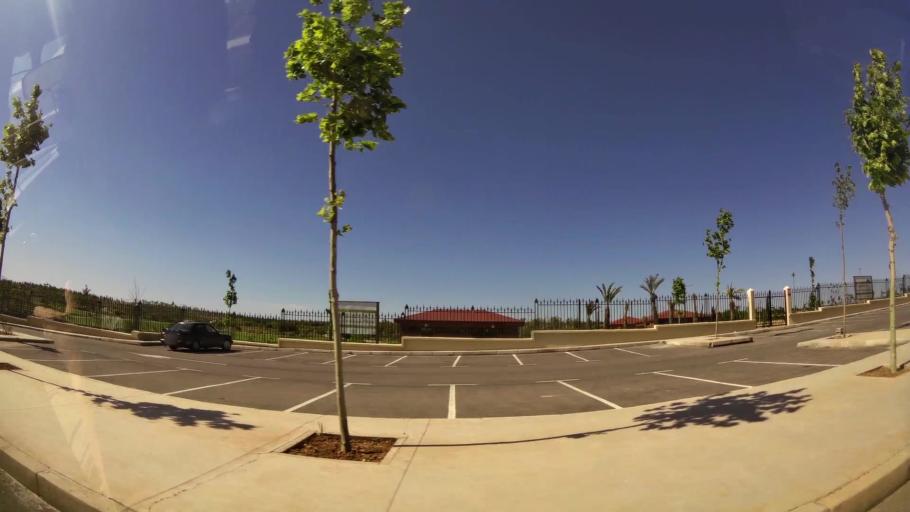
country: MA
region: Oriental
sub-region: Oujda-Angad
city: Oujda
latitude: 34.7374
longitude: -1.9216
